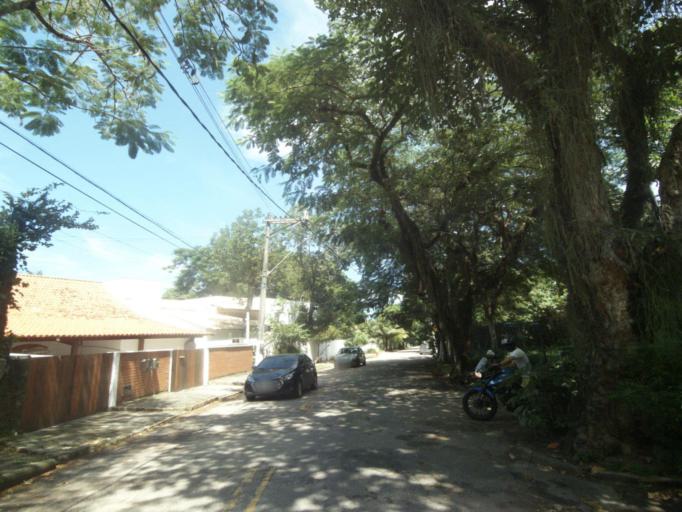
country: BR
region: Rio de Janeiro
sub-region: Niteroi
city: Niteroi
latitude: -22.9718
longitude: -43.0356
